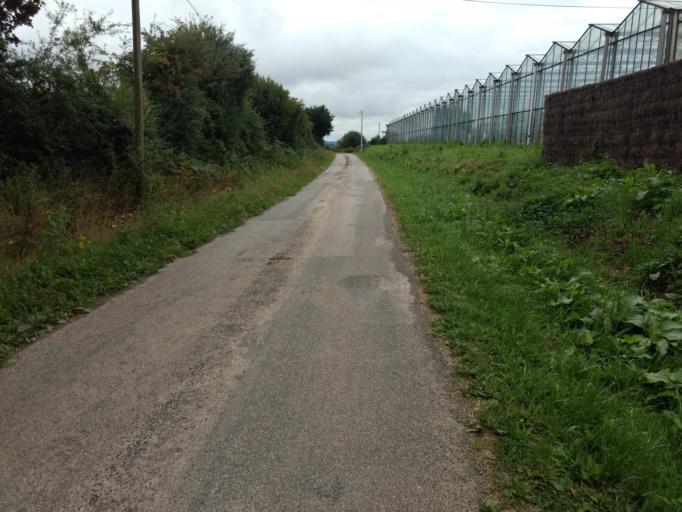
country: FR
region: Brittany
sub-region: Departement du Finistere
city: Loperhet
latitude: 48.3628
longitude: -4.2916
